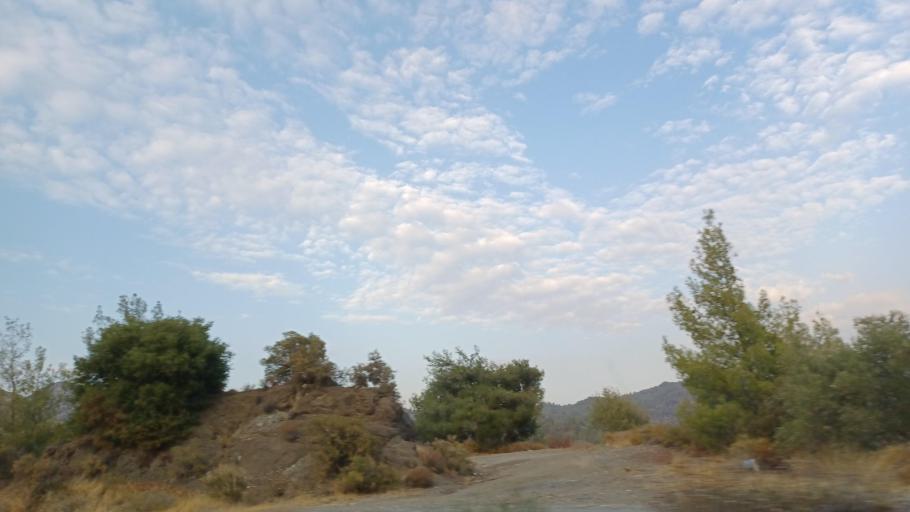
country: CY
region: Limassol
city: Pelendri
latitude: 34.8570
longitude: 32.9389
